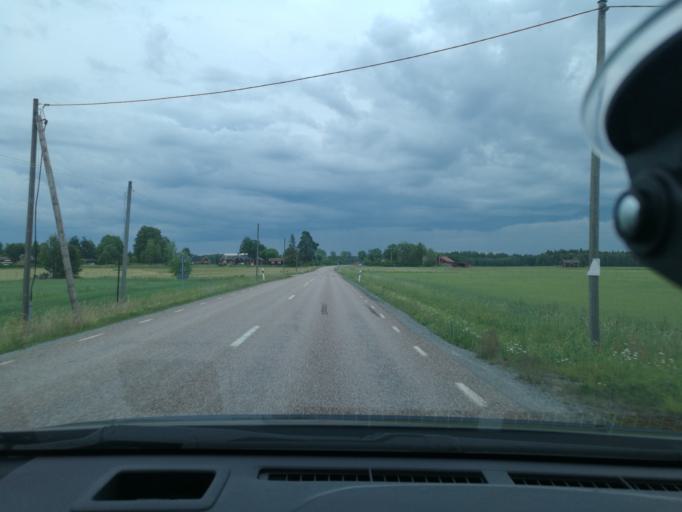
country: SE
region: Vaestmanland
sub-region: Sala Kommun
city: Sala
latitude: 59.9140
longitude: 16.4281
